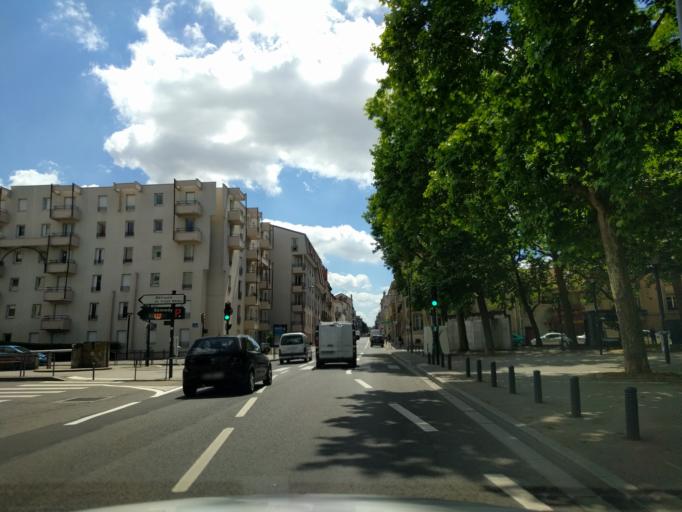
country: FR
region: Lorraine
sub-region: Departement de Meurthe-et-Moselle
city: Nancy
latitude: 48.6856
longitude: 6.1719
